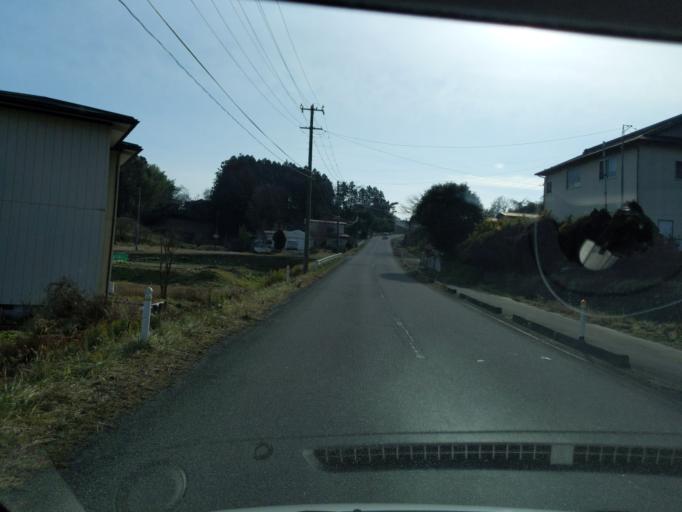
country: JP
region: Miyagi
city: Wakuya
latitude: 38.7023
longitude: 141.1577
